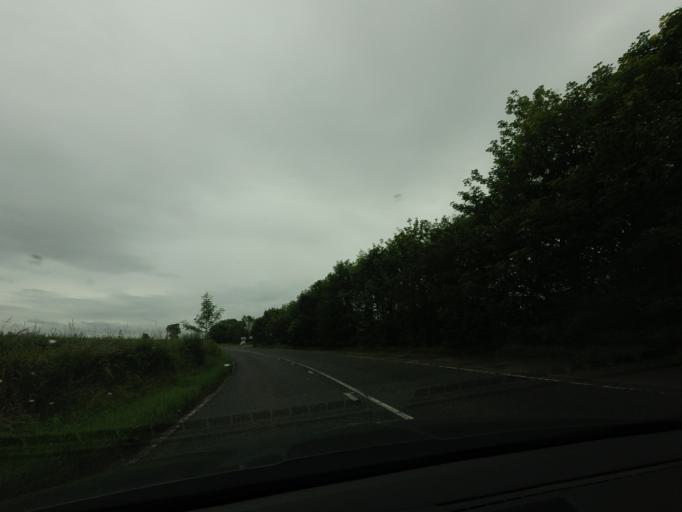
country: GB
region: Scotland
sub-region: Aberdeenshire
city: Portsoy
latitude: 57.6749
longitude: -2.6879
